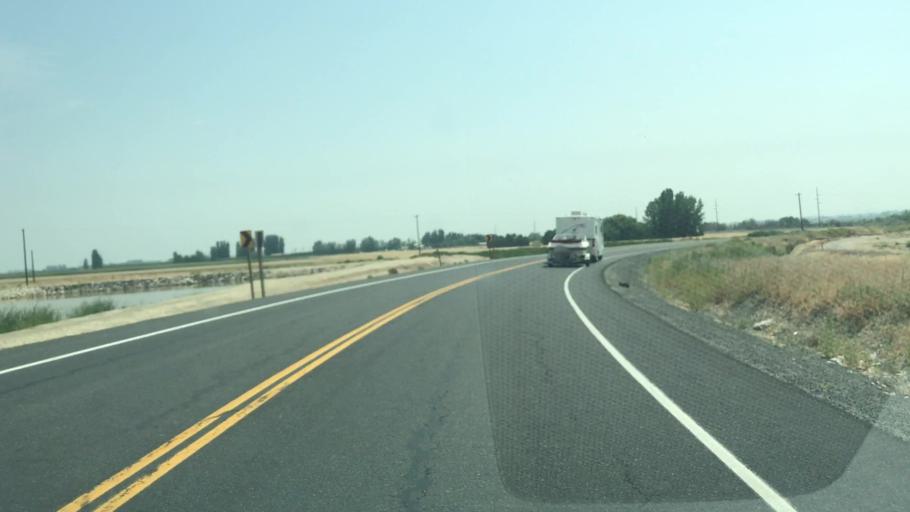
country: US
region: Washington
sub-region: Grant County
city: Quincy
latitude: 47.1636
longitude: -119.9205
